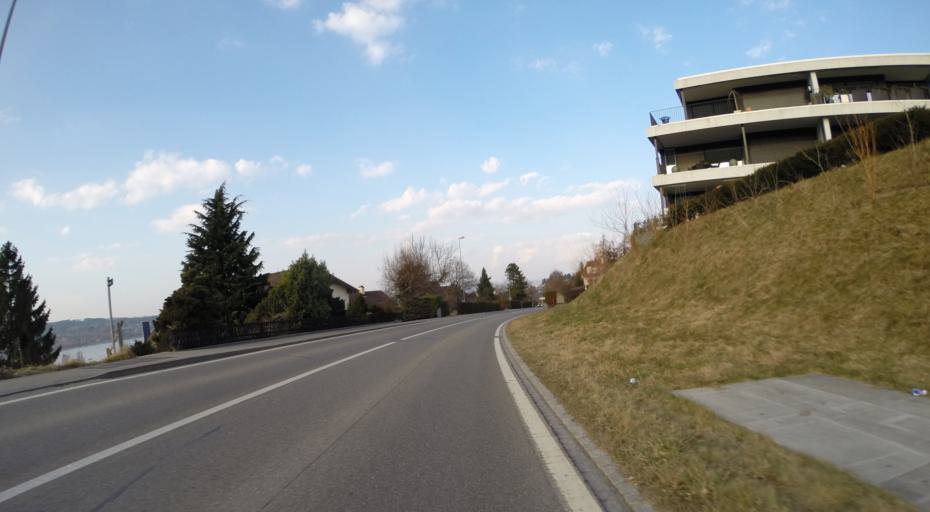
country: CH
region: Thurgau
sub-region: Frauenfeld District
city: Steckborn
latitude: 47.6602
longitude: 8.9811
